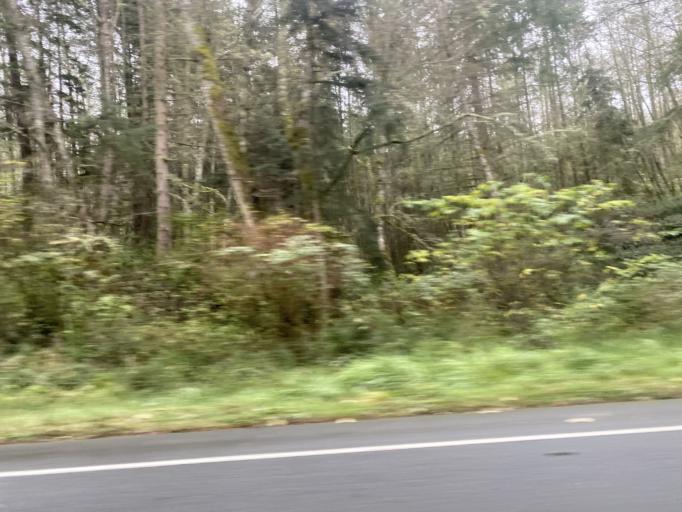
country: US
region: Washington
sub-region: Island County
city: Freeland
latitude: 48.0484
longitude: -122.5068
